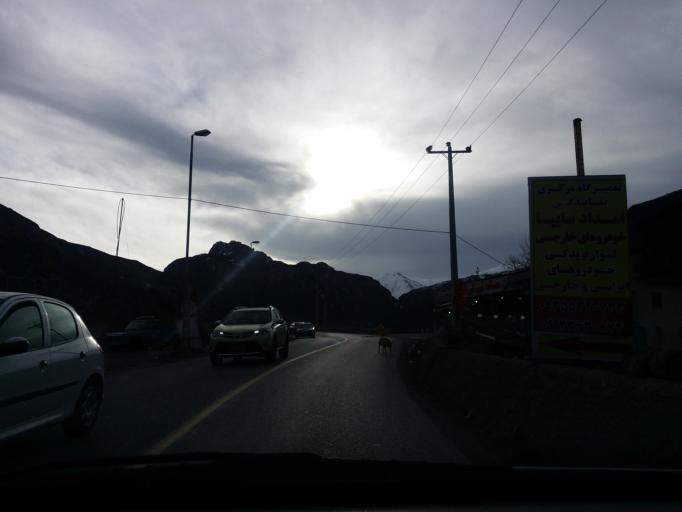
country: IR
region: Mazandaran
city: Chalus
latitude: 36.2510
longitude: 51.2832
